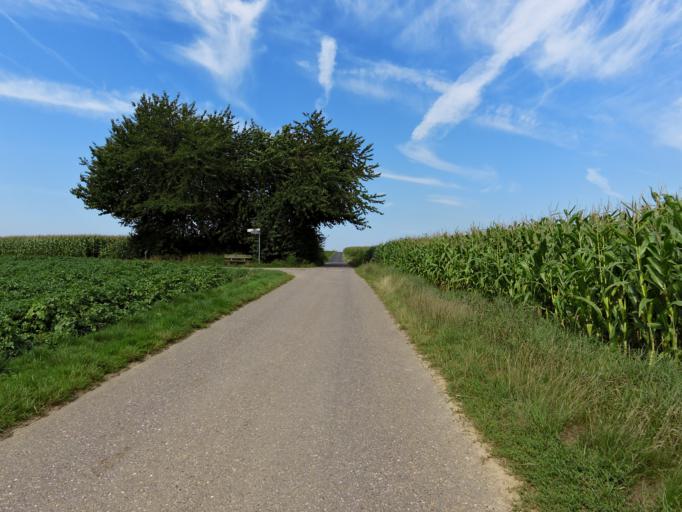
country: DE
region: North Rhine-Westphalia
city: Baesweiler
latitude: 50.9000
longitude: 6.2013
